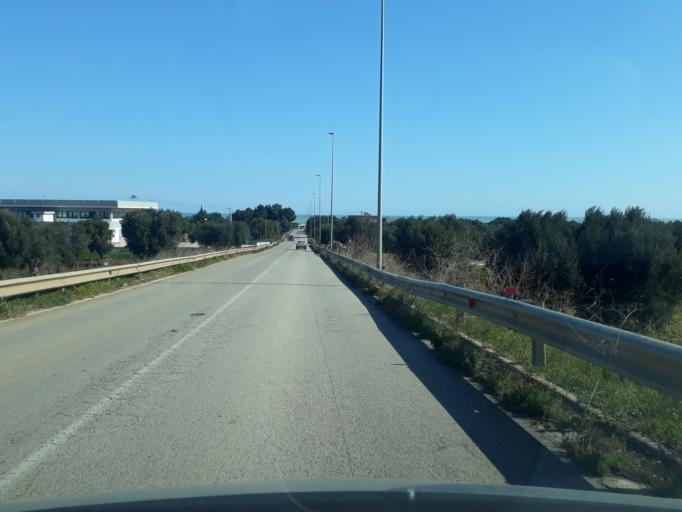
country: IT
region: Apulia
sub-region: Provincia di Brindisi
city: Fasano
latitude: 40.8988
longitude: 17.3384
